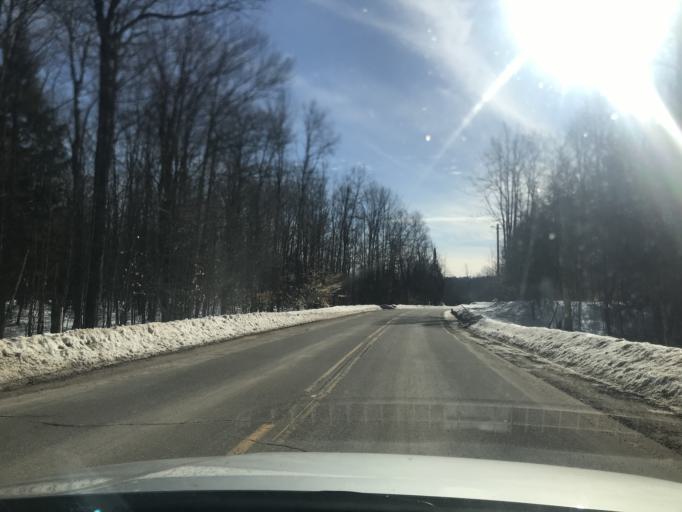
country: US
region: Michigan
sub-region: Dickinson County
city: Kingsford
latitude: 45.4162
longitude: -88.3952
